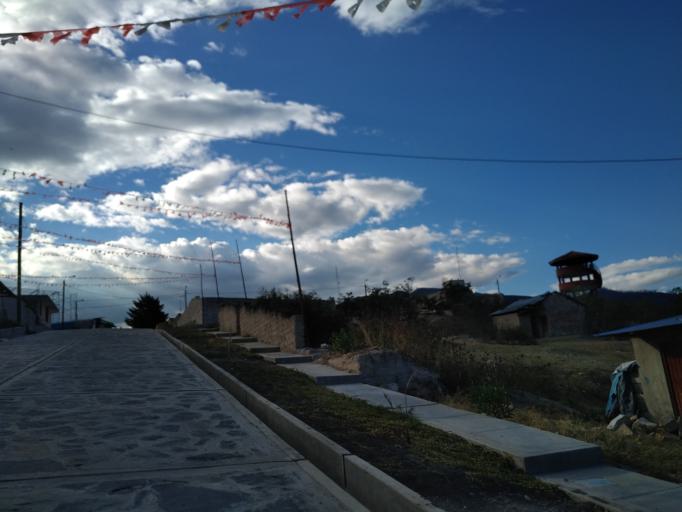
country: PE
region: Amazonas
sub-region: Provincia de Luya
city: Tingo
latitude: -6.3725
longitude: -77.9086
